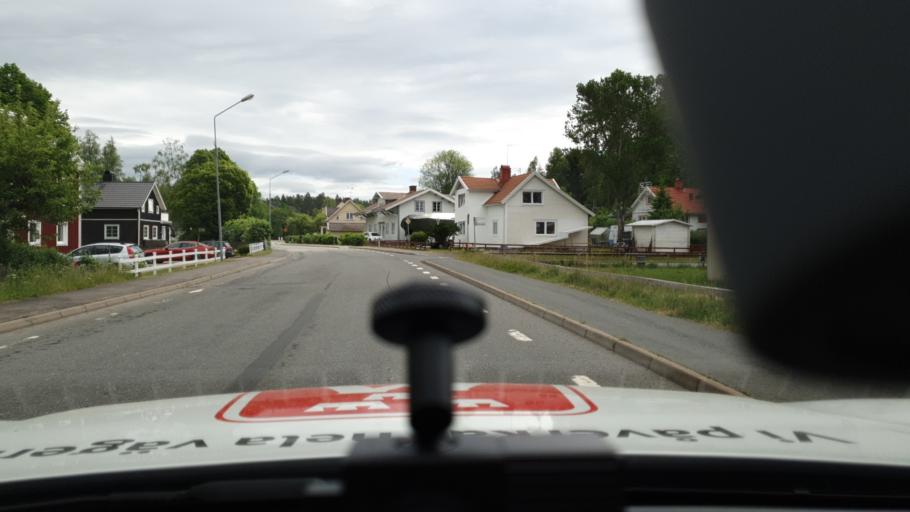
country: SE
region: Joenkoeping
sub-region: Mullsjo Kommun
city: Mullsjoe
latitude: 57.9859
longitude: 13.7726
